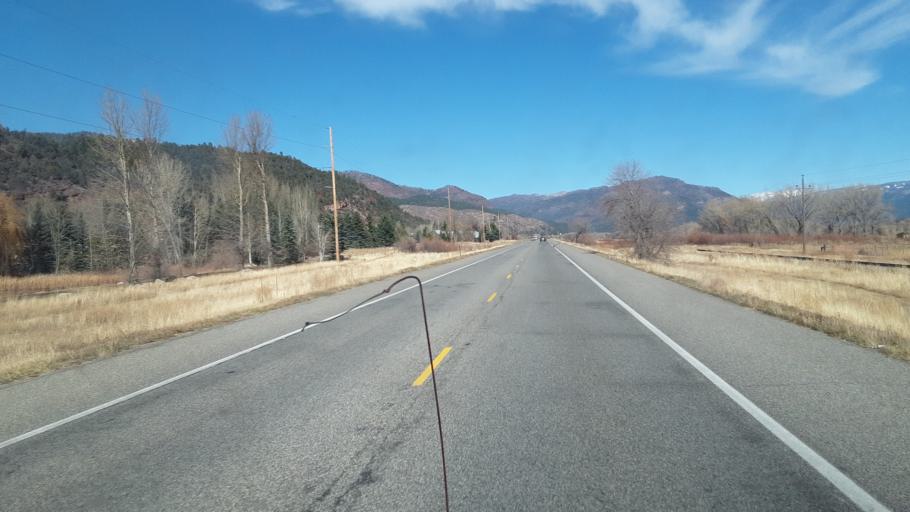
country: US
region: Colorado
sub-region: La Plata County
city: Durango
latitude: 37.3537
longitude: -107.8521
